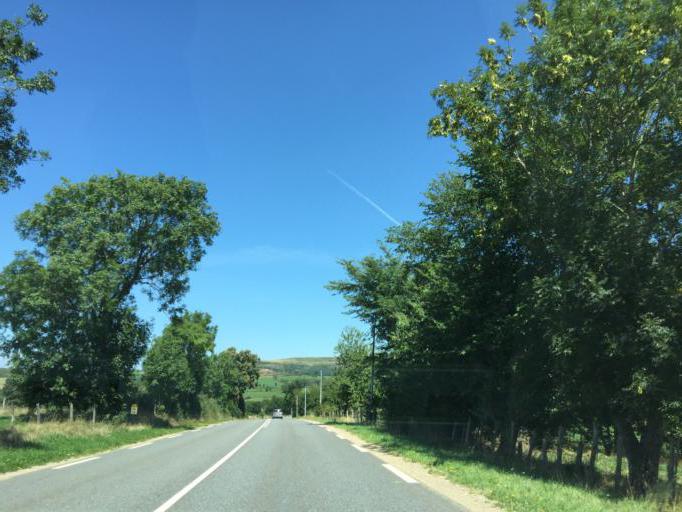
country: FR
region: Midi-Pyrenees
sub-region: Departement de l'Aveyron
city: Laguiole
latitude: 44.6417
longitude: 2.8403
